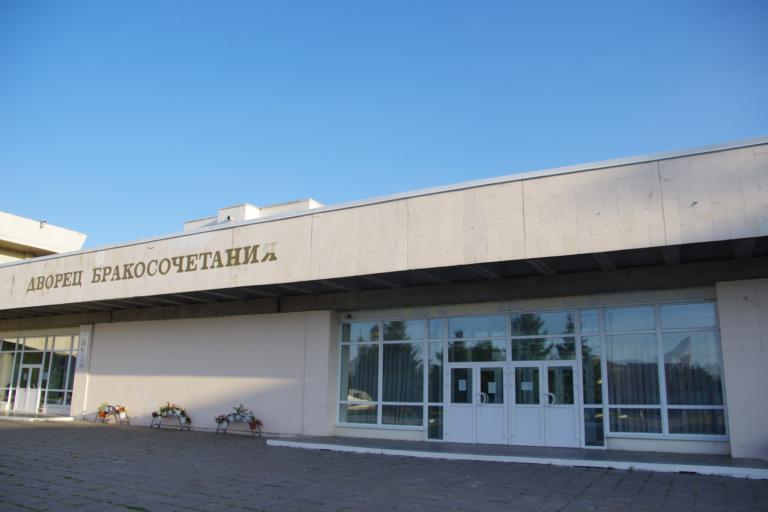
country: RU
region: Samara
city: Tol'yatti
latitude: 53.5183
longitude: 49.2738
